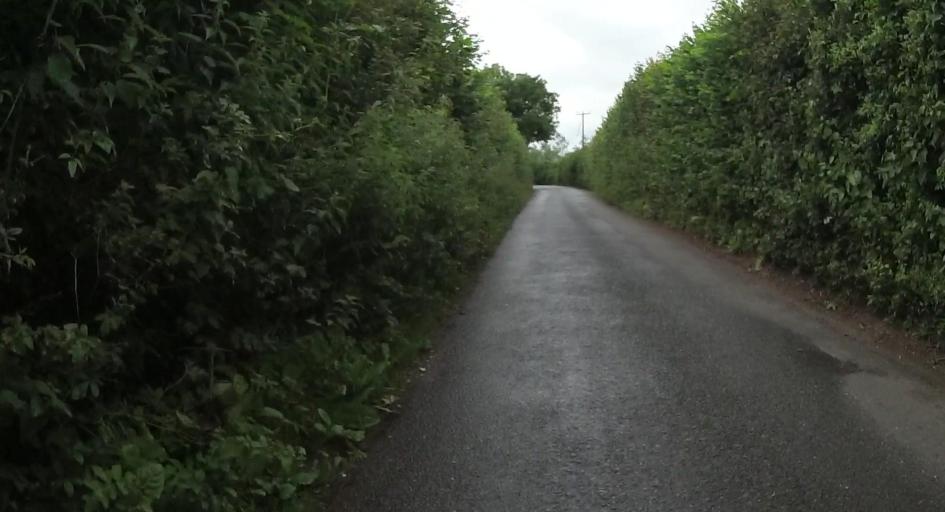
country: GB
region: England
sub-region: Hampshire
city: Andover
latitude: 51.2470
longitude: -1.4114
